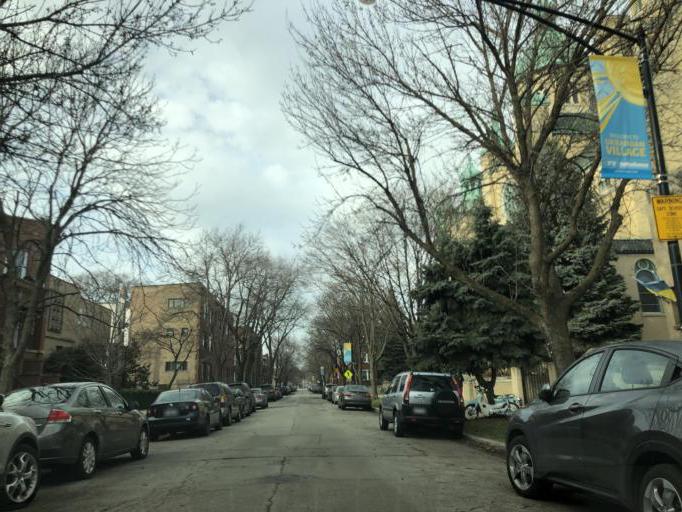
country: US
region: Illinois
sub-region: Cook County
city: Chicago
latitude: 41.8968
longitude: -87.6832
